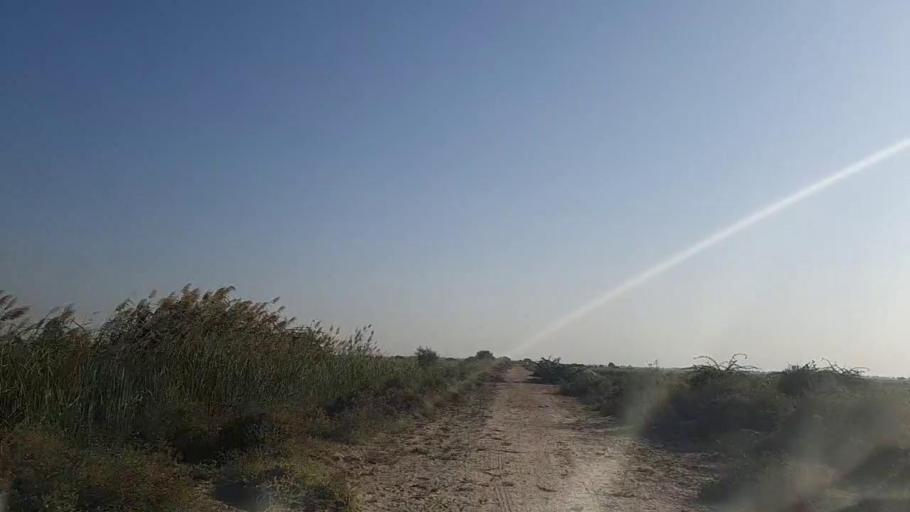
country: PK
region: Sindh
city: Jati
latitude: 24.3934
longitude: 68.2302
